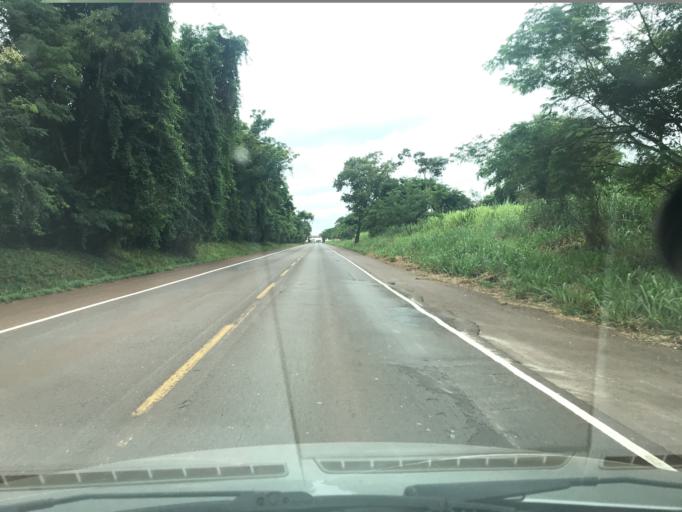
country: BR
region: Parana
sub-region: Terra Boa
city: Terra Boa
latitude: -23.6030
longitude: -52.3401
